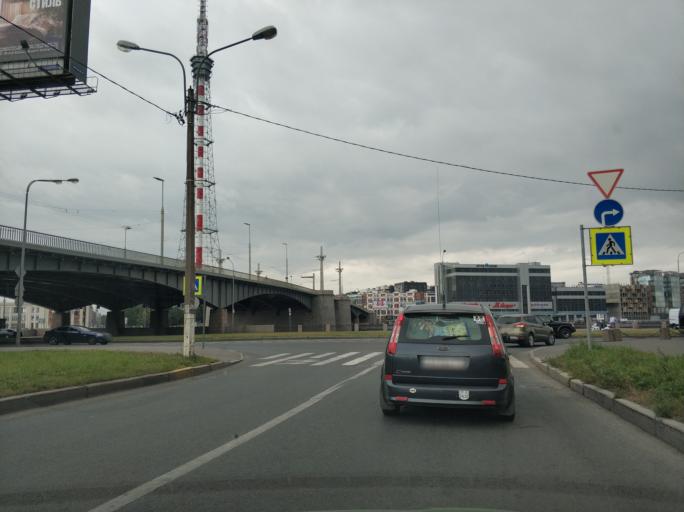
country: RU
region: St.-Petersburg
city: Petrogradka
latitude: 59.9799
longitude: 30.3238
